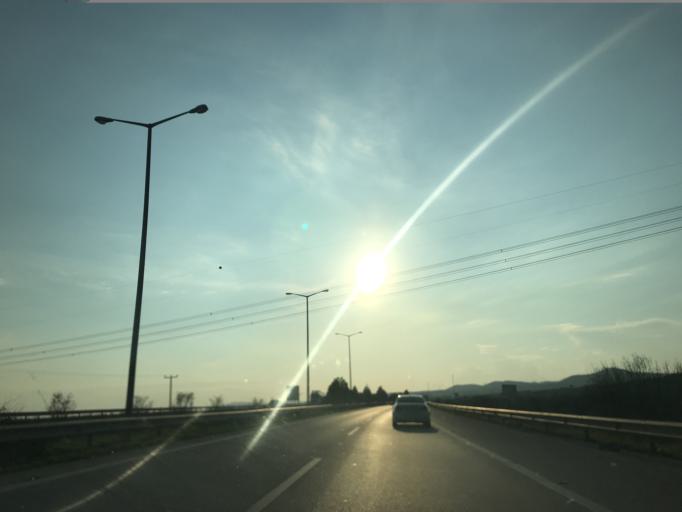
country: TR
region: Osmaniye
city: Toprakkale
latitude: 36.9685
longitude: 36.0521
